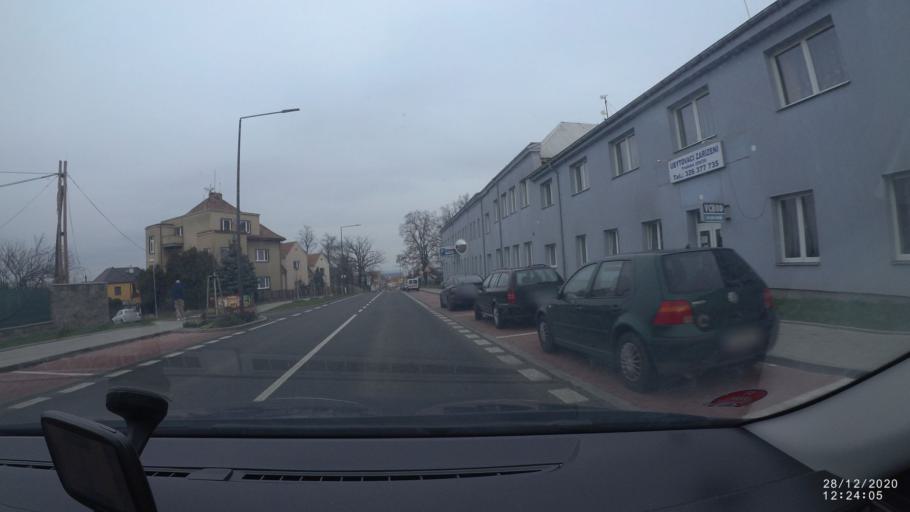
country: CZ
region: Central Bohemia
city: Brandys nad Labem-Stara Boleslav
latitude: 50.1801
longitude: 14.6559
